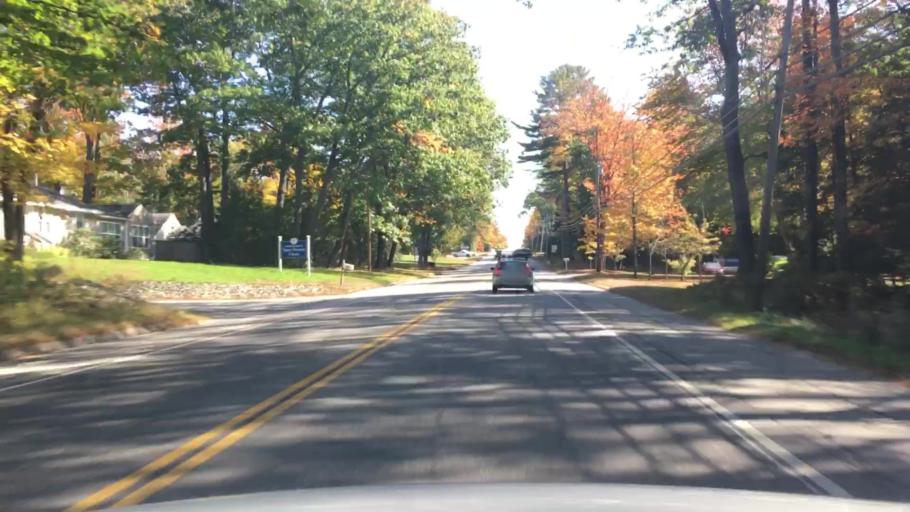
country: US
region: Maine
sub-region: Sagadahoc County
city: Topsham
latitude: 43.9499
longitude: -69.9918
